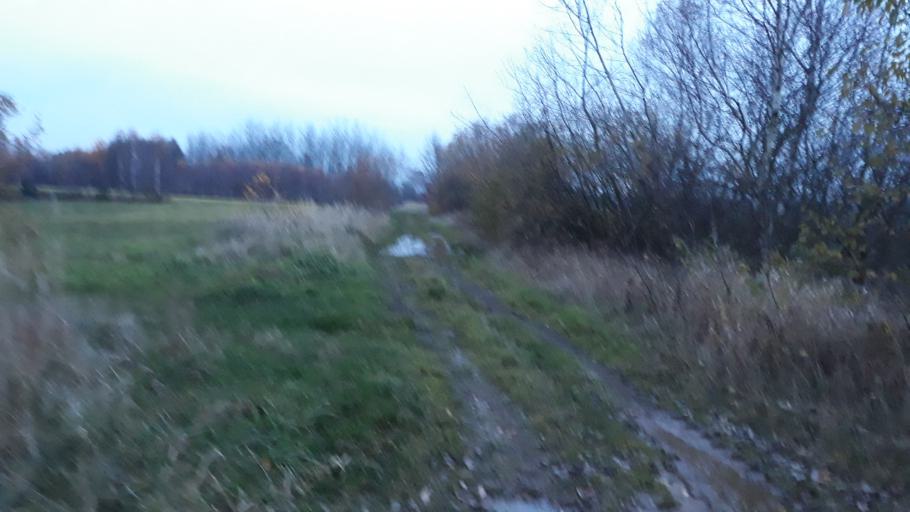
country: PL
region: Lublin Voivodeship
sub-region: Powiat janowski
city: Dzwola
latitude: 50.6645
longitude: 22.5918
